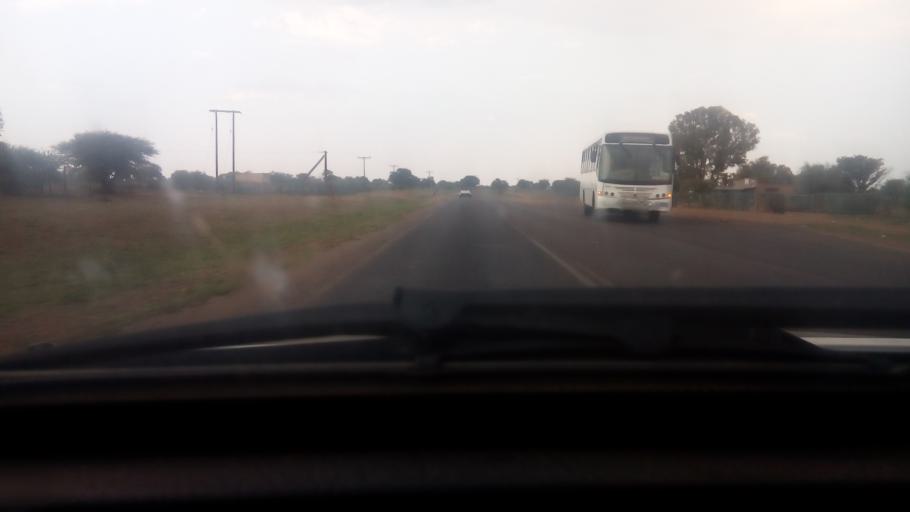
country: BW
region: Kweneng
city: Metsemotlhaba
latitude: -24.4774
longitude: 25.7241
